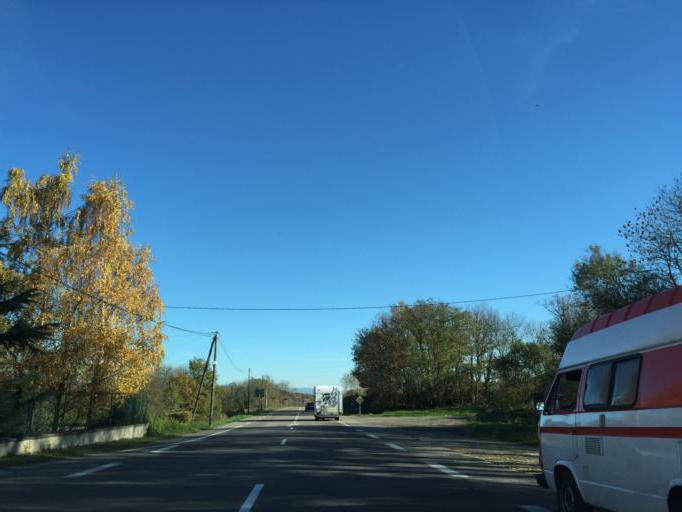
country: FR
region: Rhone-Alpes
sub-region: Departement de la Loire
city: Saint-Germain-Laval
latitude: 45.8982
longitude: 4.0167
